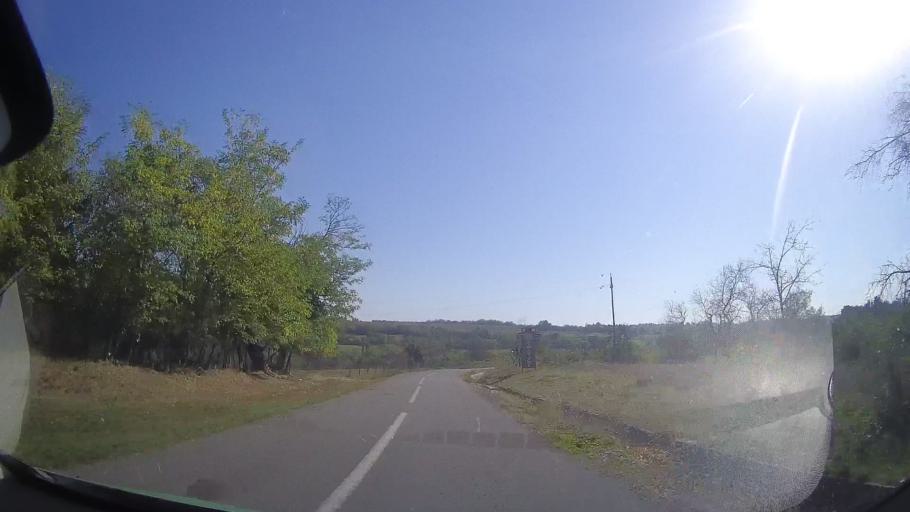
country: RO
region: Timis
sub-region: Comuna Bara
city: Bara
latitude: 45.8944
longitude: 21.9165
